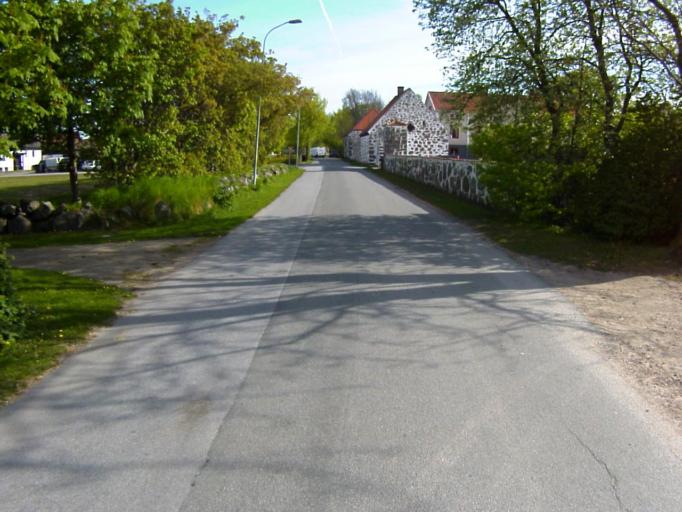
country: SE
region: Skane
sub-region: Kristianstads Kommun
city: Fjalkinge
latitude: 56.0380
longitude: 14.2770
